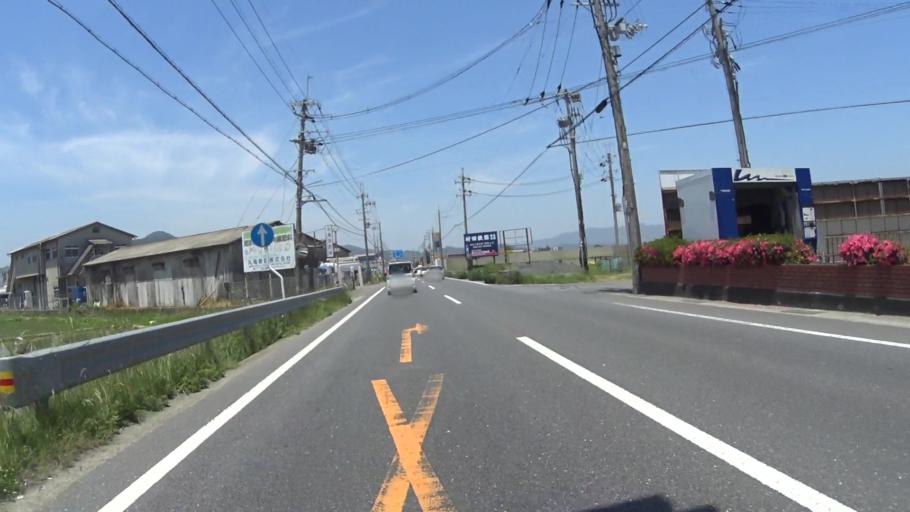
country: JP
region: Kyoto
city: Kameoka
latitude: 35.0196
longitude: 135.5615
